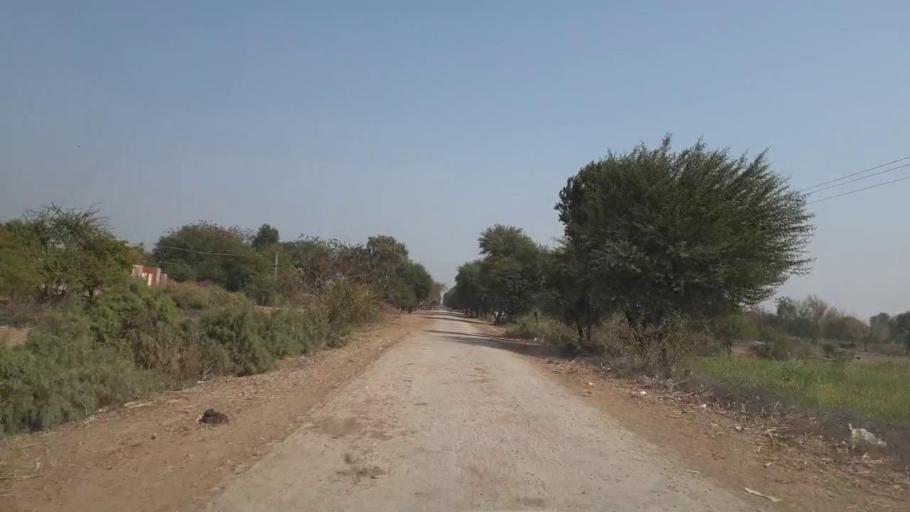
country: PK
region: Sindh
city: Mirpur Khas
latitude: 25.6632
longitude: 69.1766
